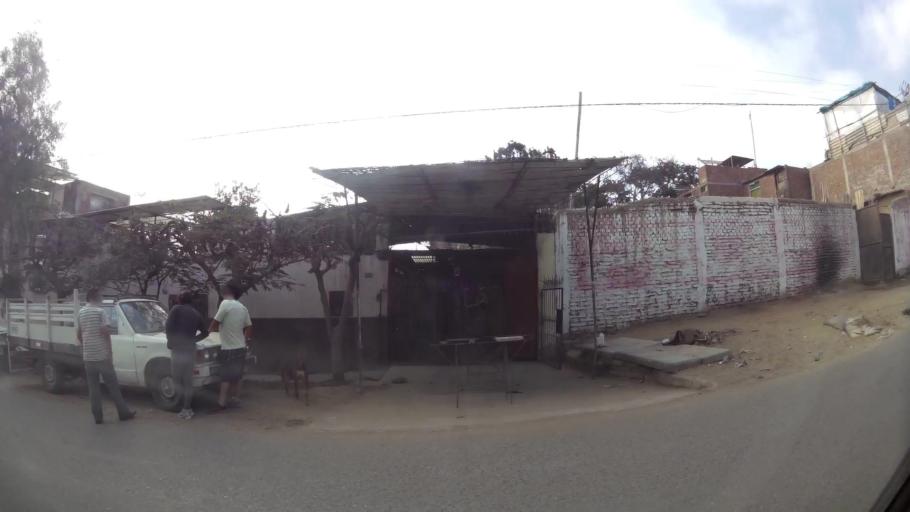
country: PE
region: La Libertad
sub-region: Provincia de Trujillo
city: La Esperanza
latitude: -8.0726
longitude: -79.0451
